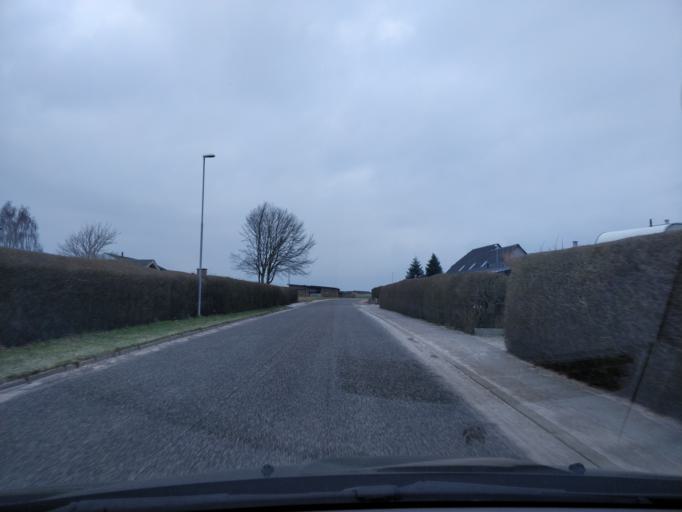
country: DK
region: South Denmark
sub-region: Vejle Kommune
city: Vejle
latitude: 55.7649
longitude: 9.5461
